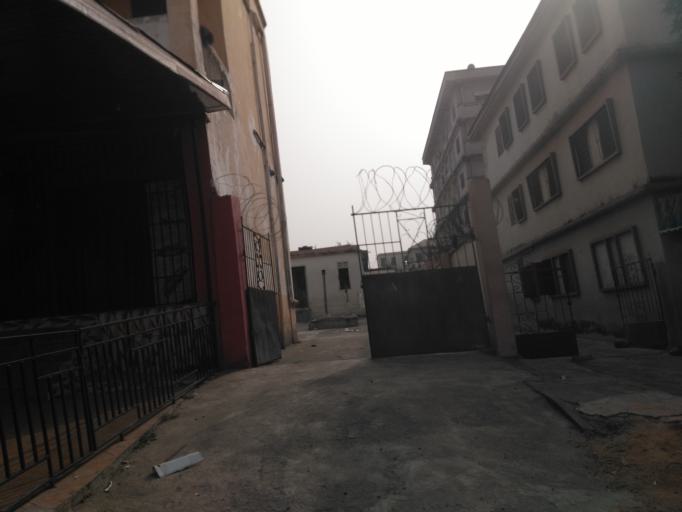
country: GH
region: Ashanti
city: Kumasi
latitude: 6.6986
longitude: -1.6119
